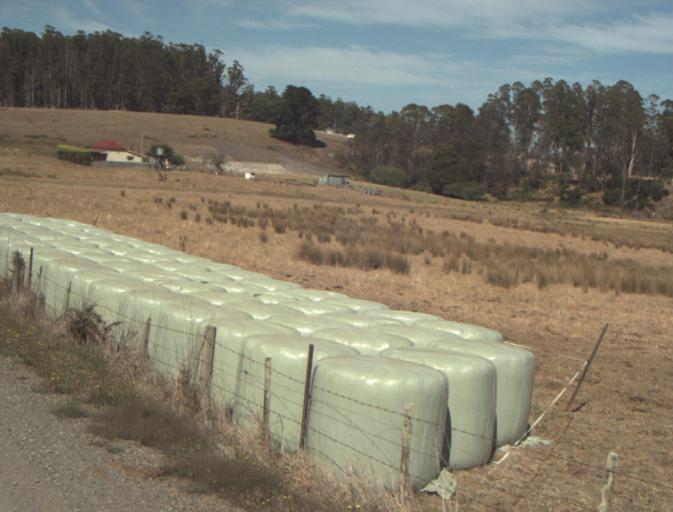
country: AU
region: Tasmania
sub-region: Launceston
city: Mayfield
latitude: -41.2250
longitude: 147.2369
